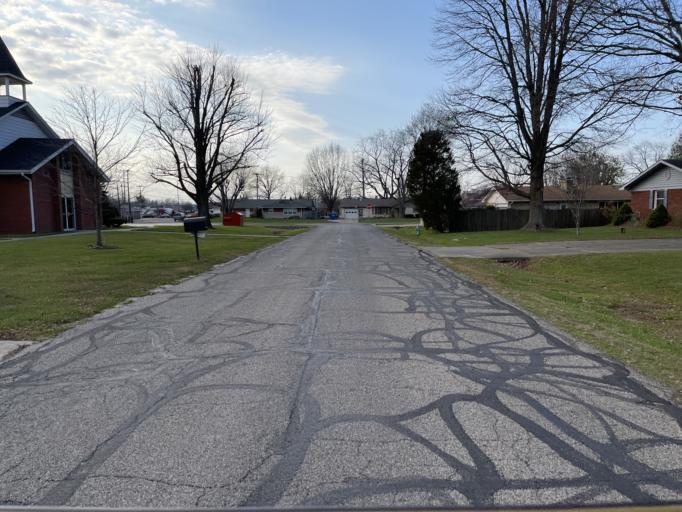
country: US
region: Indiana
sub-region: Hendricks County
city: Avon
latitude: 39.7639
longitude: -86.3974
